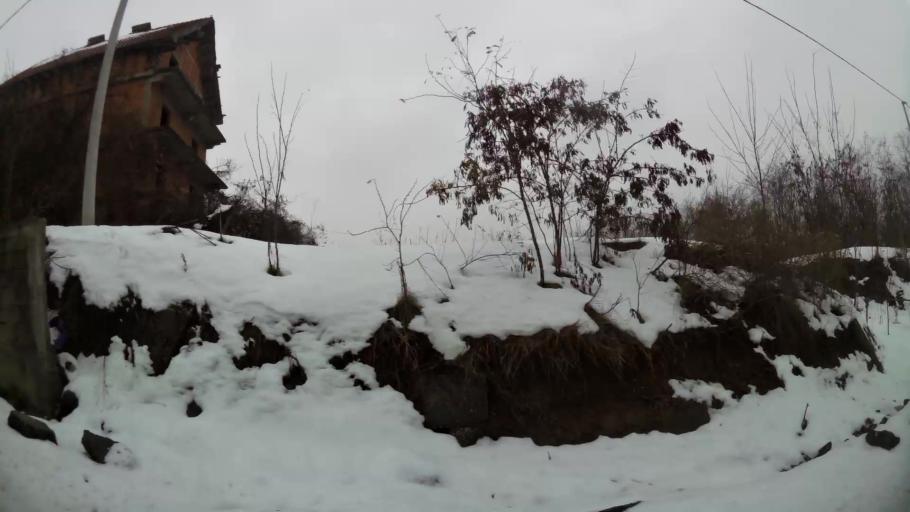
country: RS
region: Central Serbia
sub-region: Belgrade
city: Zvezdara
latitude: 44.7483
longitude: 20.5095
